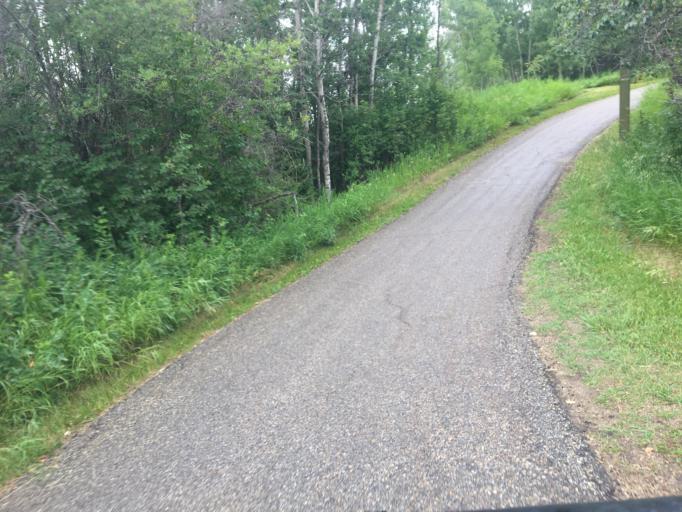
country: CA
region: Alberta
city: Grande Prairie
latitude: 55.1617
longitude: -118.8069
